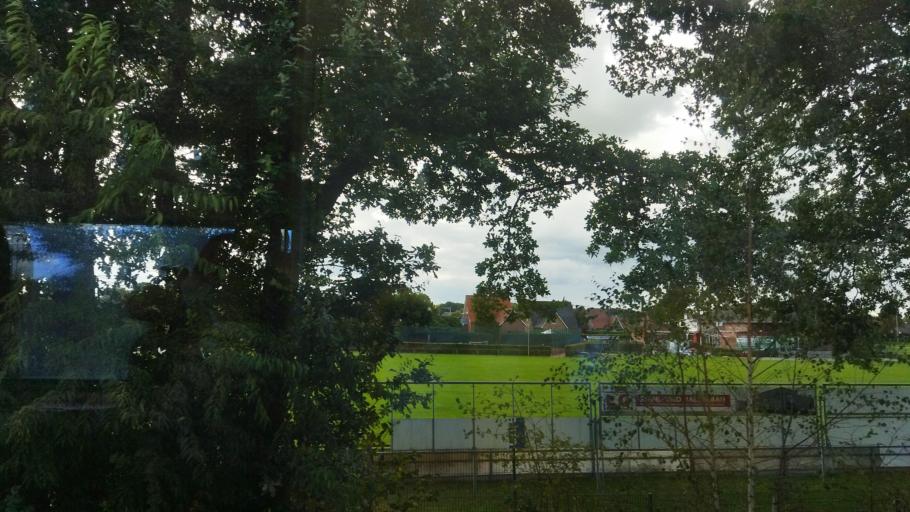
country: DE
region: Lower Saxony
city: Emsburen
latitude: 52.3964
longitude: 7.3066
